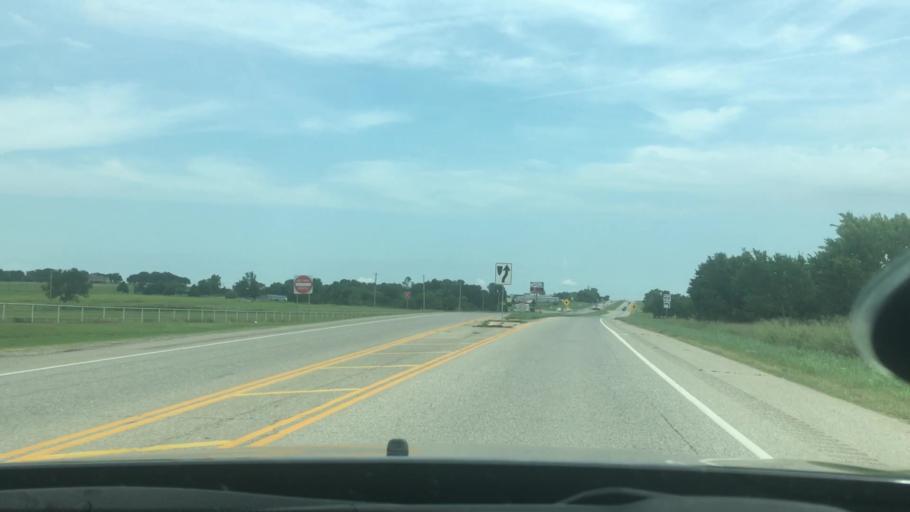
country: US
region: Oklahoma
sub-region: Seminole County
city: Seminole
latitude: 35.1829
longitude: -96.6749
